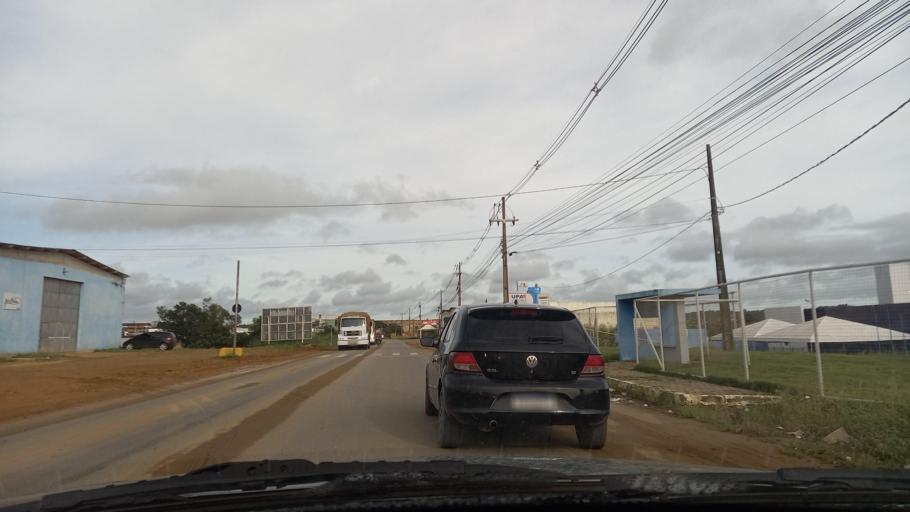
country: BR
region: Pernambuco
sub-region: Vitoria De Santo Antao
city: Vitoria de Santo Antao
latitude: -8.1213
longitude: -35.3268
